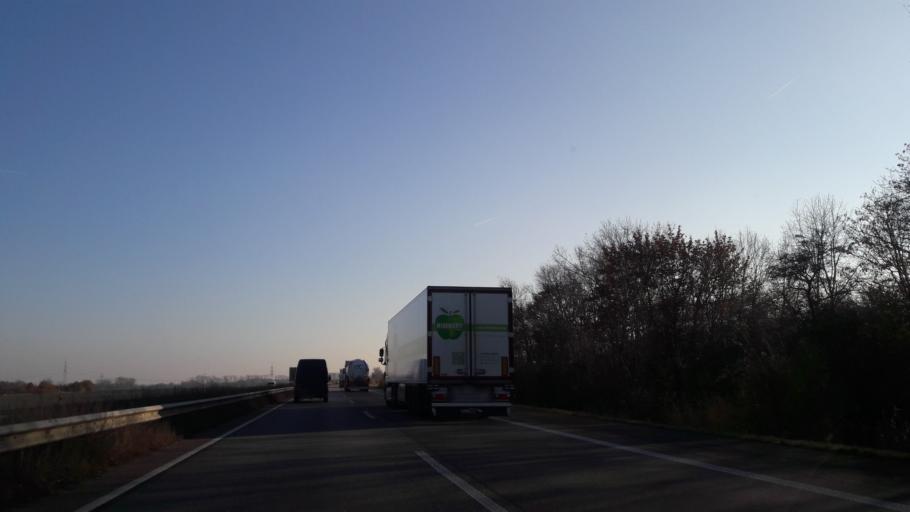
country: DE
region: Rheinland-Pfalz
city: Dannstadt-Schauernheim
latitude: 49.4287
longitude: 8.3324
